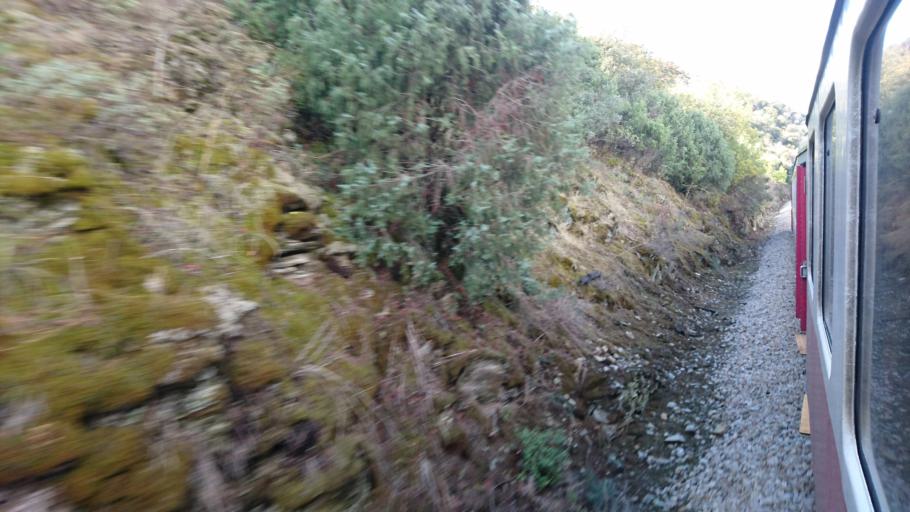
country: PT
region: Guarda
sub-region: Vila Nova de Foz Coa
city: Custoias
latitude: 41.1432
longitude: -7.2517
